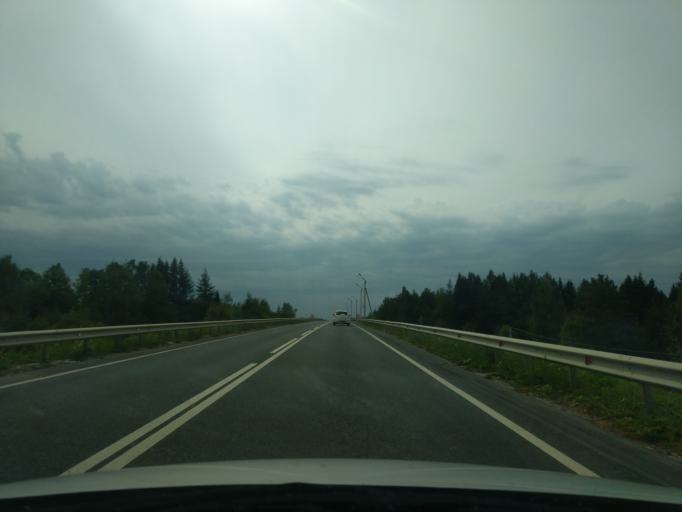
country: RU
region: Kostroma
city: Manturovo
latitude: 58.3311
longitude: 44.7163
